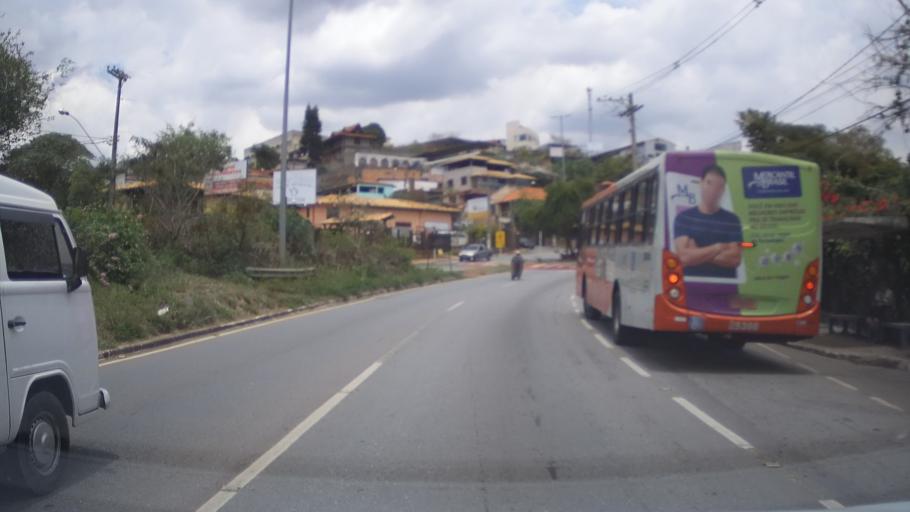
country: BR
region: Minas Gerais
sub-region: Nova Lima
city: Nova Lima
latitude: -19.9996
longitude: -43.8872
